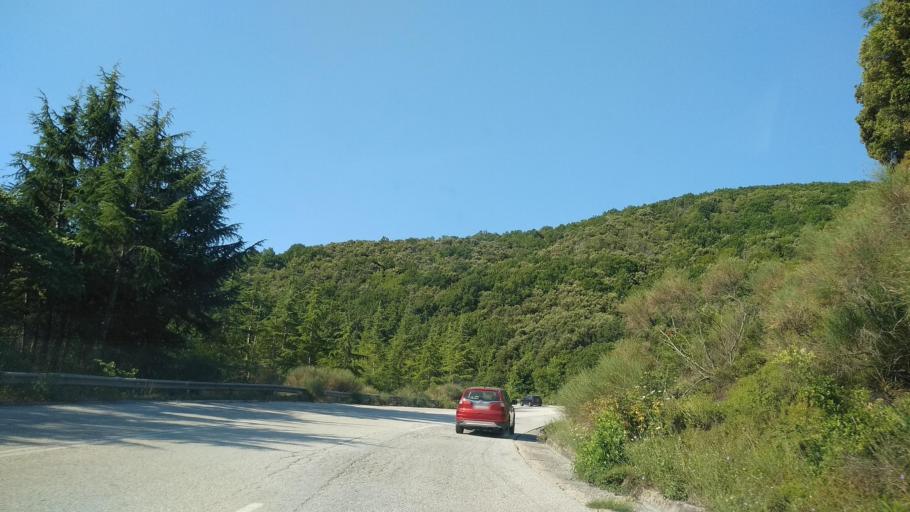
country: GR
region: Central Macedonia
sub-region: Nomos Chalkidikis
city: Stratonion
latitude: 40.5367
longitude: 23.8283
